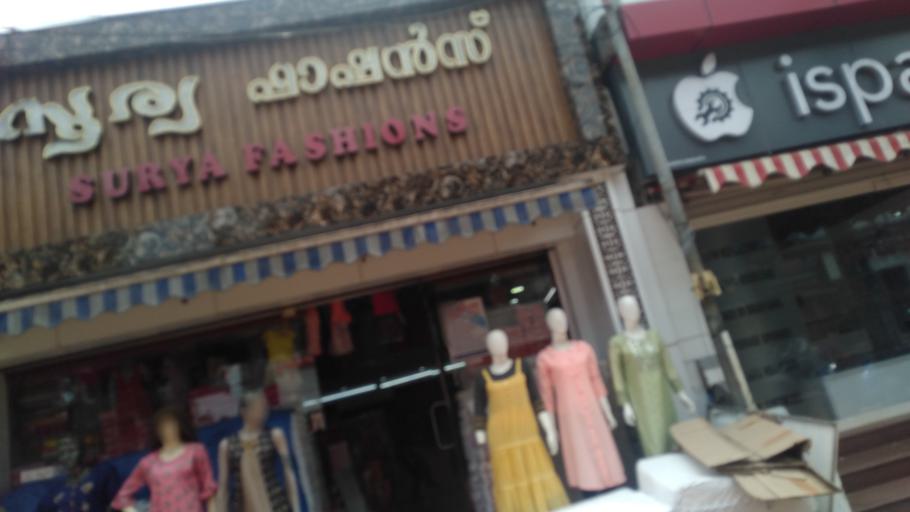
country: IN
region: Kerala
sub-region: Alappuzha
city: Alleppey
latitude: 9.4960
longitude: 76.3427
